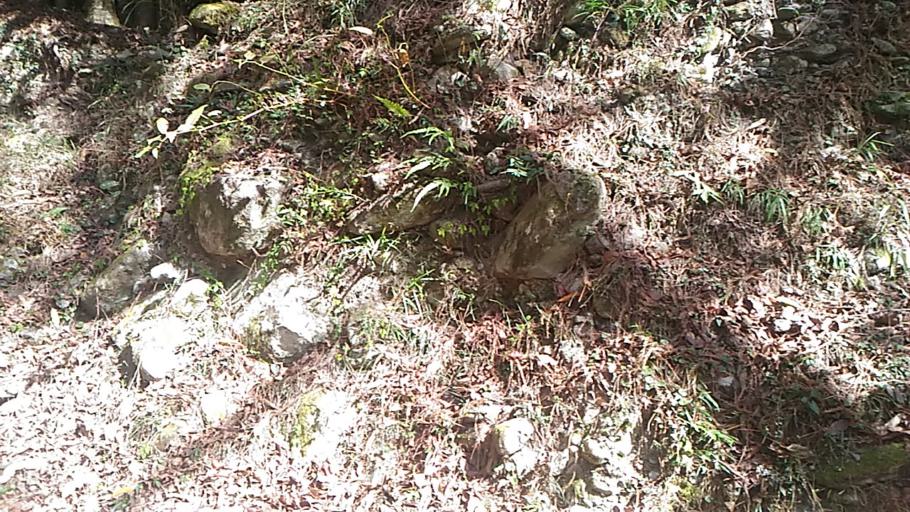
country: TW
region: Taiwan
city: Daxi
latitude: 24.3984
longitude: 121.3081
